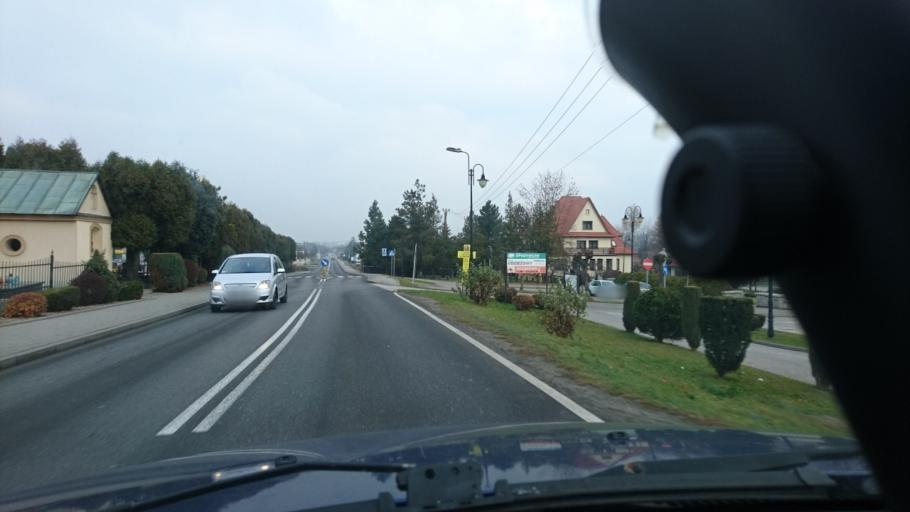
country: PL
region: Silesian Voivodeship
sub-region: Powiat bielski
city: Pisarzowice
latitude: 49.8791
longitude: 19.1372
